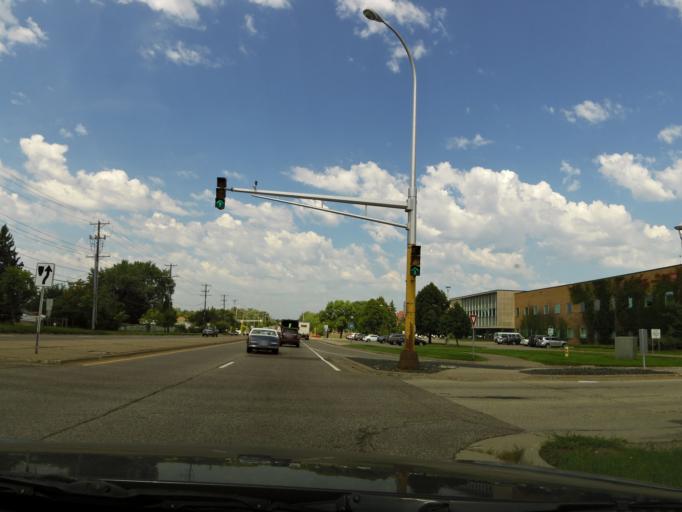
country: US
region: Minnesota
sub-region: Ramsey County
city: Maplewood
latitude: 44.9538
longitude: -93.0048
